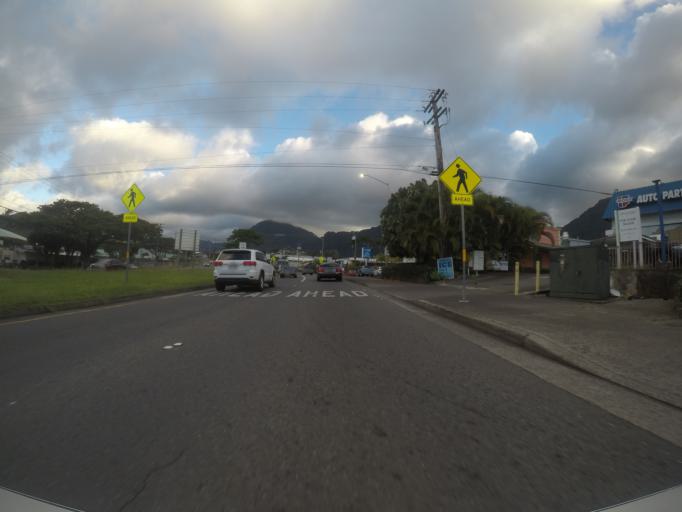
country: US
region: Hawaii
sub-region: Honolulu County
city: Kane'ohe
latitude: 21.4020
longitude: -157.7999
